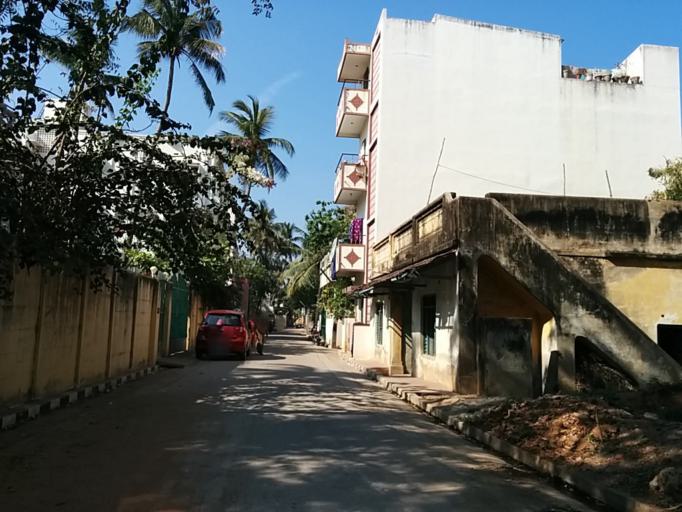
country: IN
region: Pondicherry
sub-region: Puducherry
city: Puducherry
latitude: 11.9464
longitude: 79.8361
